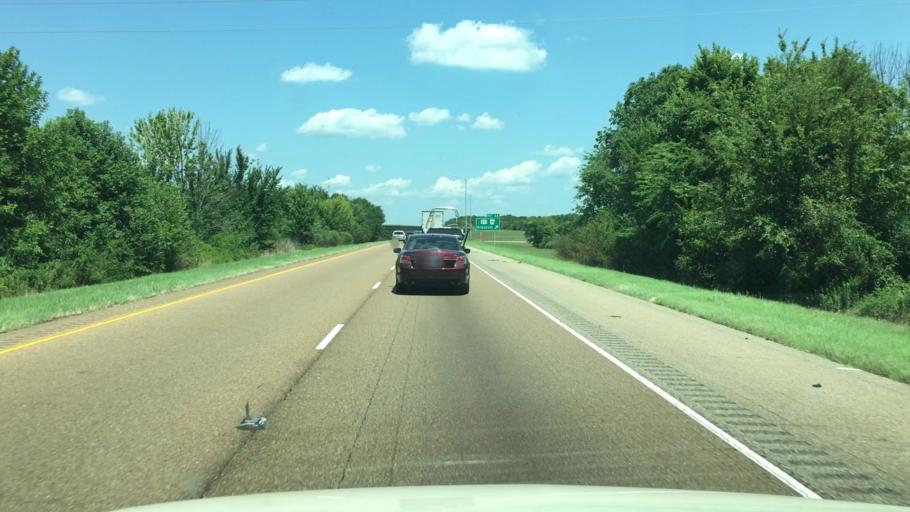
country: US
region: Arkansas
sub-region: Nevada County
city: Prescott
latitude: 33.8075
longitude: -93.4272
